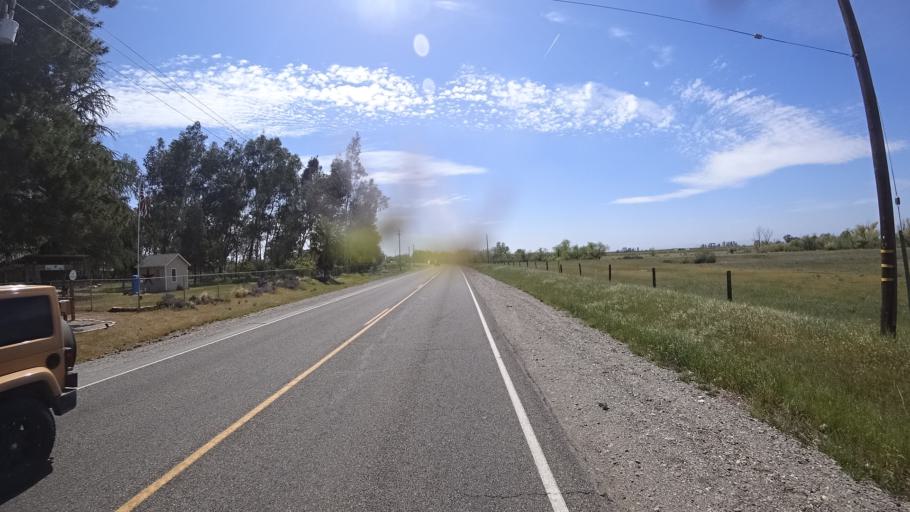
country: US
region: California
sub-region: Glenn County
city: Willows
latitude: 39.6290
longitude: -122.1976
